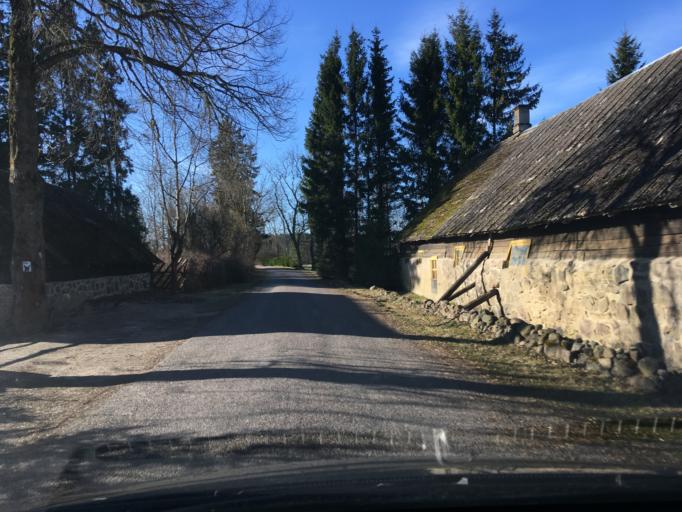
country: EE
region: Laeaene
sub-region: Lihula vald
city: Lihula
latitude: 58.5842
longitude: 23.7060
